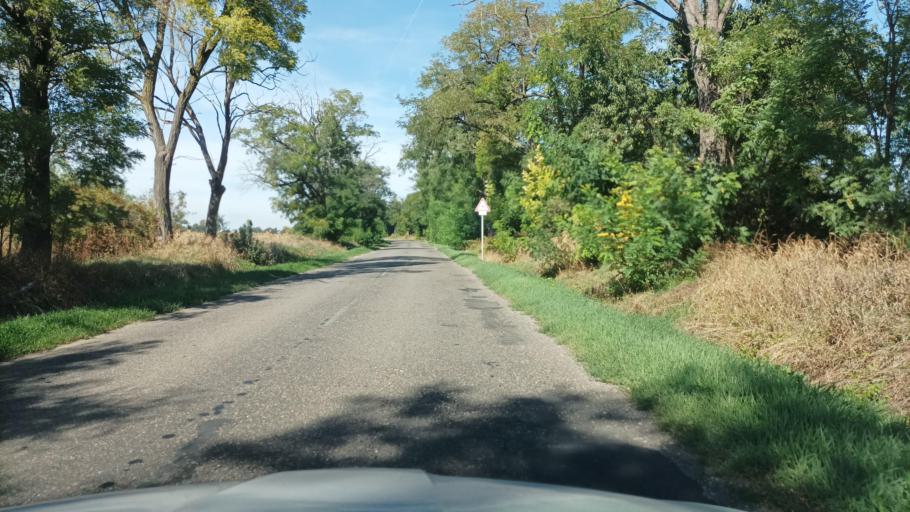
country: HU
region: Pest
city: Vacszentlaszlo
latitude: 47.5587
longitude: 19.5650
